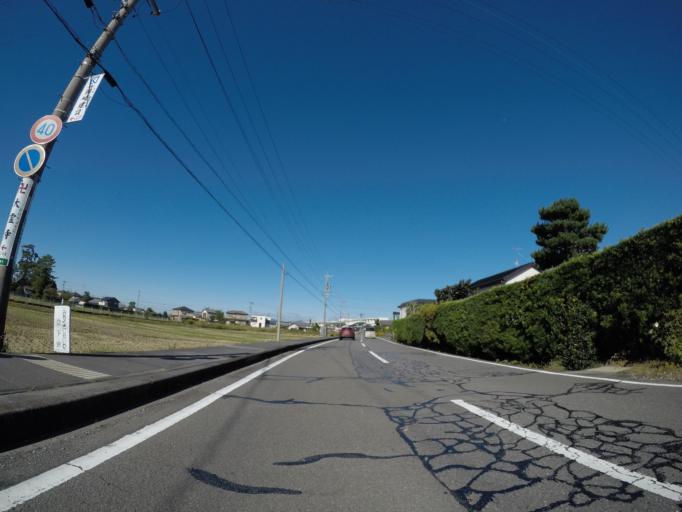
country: JP
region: Shizuoka
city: Fujieda
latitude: 34.8249
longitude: 138.2543
